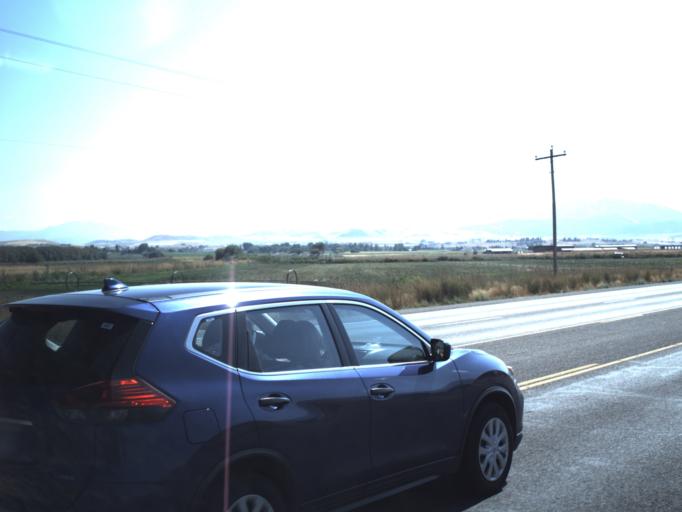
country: US
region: Utah
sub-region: Cache County
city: Wellsville
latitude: 41.6652
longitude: -111.8935
